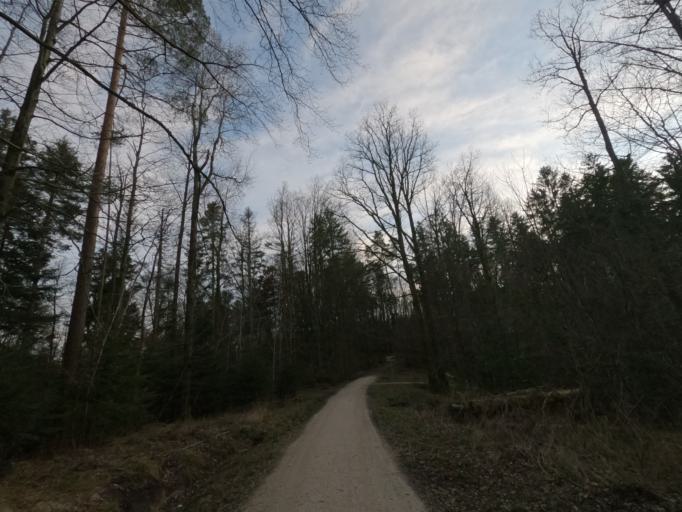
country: DE
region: Baden-Wuerttemberg
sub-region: Regierungsbezirk Stuttgart
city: Eislingen
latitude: 48.7246
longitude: 9.7083
